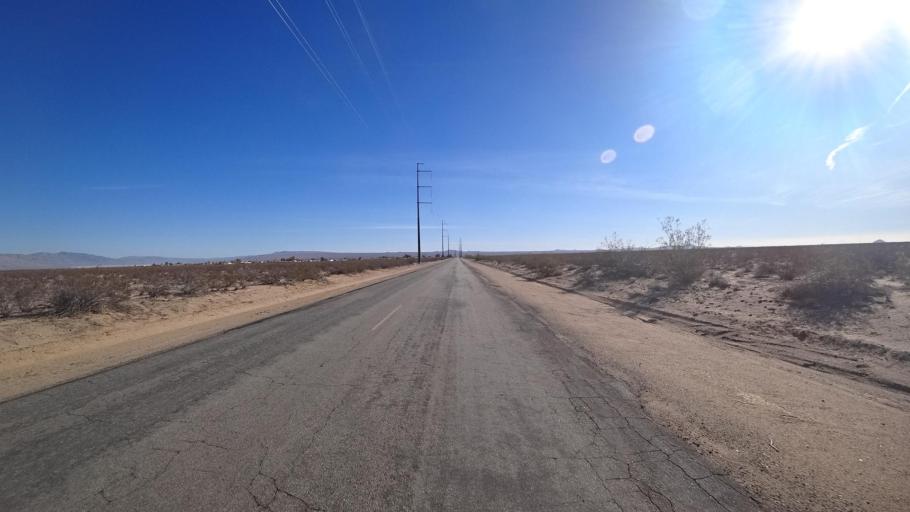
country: US
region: California
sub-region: Kern County
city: California City
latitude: 35.1986
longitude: -118.0278
